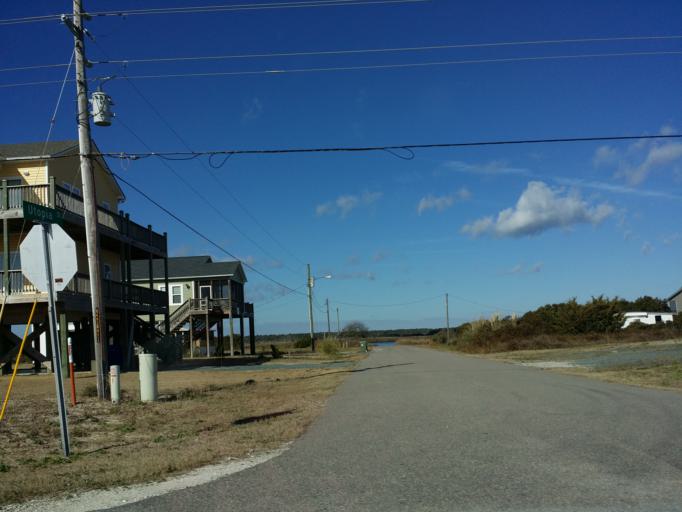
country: US
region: North Carolina
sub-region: Pender County
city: Surf City
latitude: 34.4490
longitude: -77.5071
